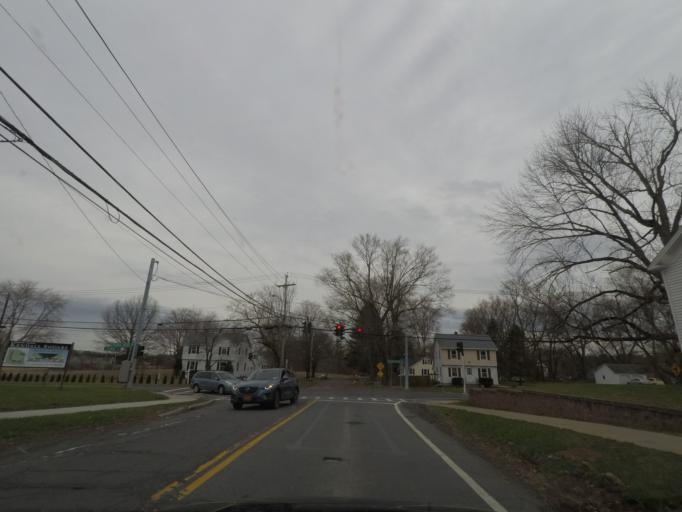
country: US
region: New York
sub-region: Albany County
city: Delmar
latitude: 42.6016
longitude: -73.8182
